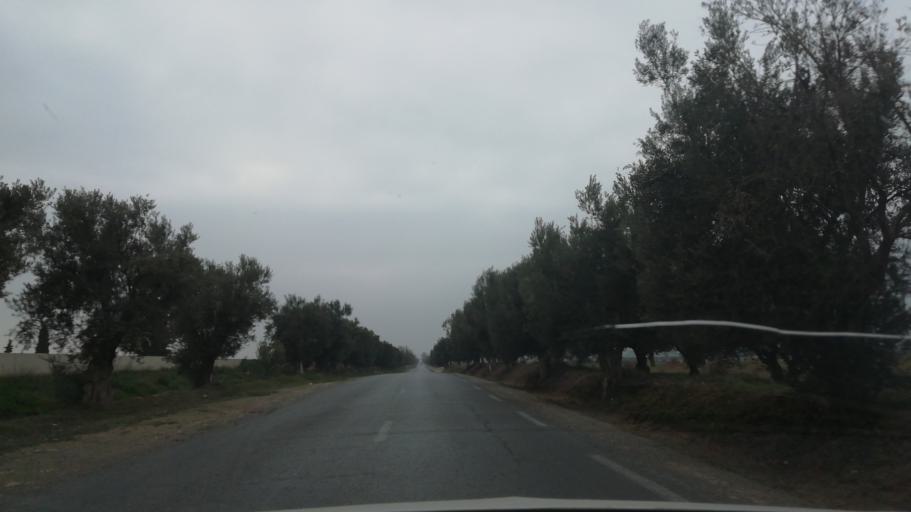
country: DZ
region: Sidi Bel Abbes
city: Sfizef
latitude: 35.2255
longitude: -0.2757
